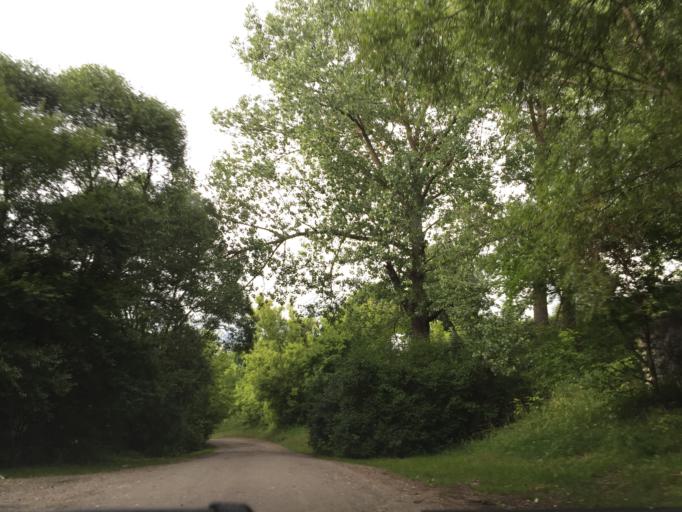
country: PL
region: Podlasie
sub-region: Suwalki
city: Suwalki
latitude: 54.1170
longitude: 22.9243
